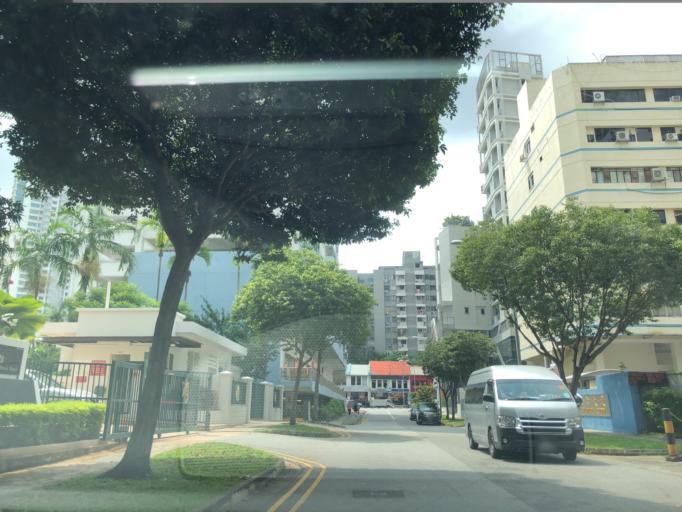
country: SG
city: Singapore
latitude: 1.3272
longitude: 103.8491
